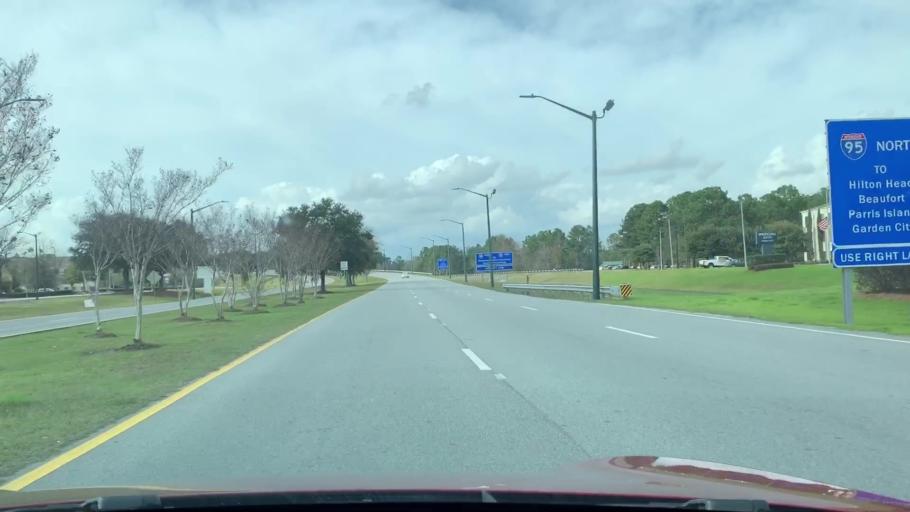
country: US
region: Georgia
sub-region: Chatham County
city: Pooler
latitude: 32.1397
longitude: -81.2345
